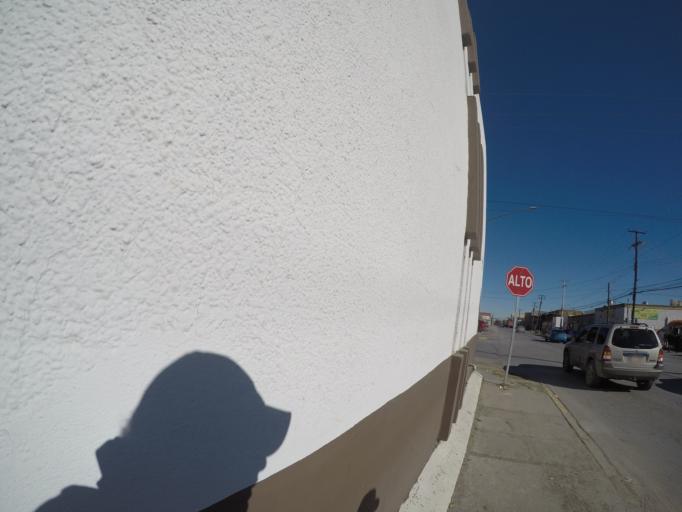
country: MX
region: Chihuahua
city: Ciudad Juarez
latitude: 31.7346
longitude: -106.4589
